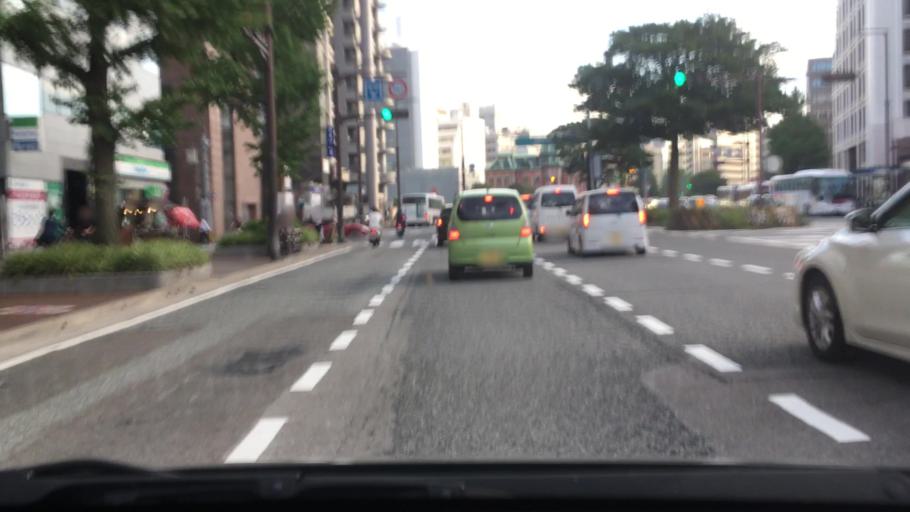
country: JP
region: Fukuoka
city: Fukuoka-shi
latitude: 33.5947
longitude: 130.4038
